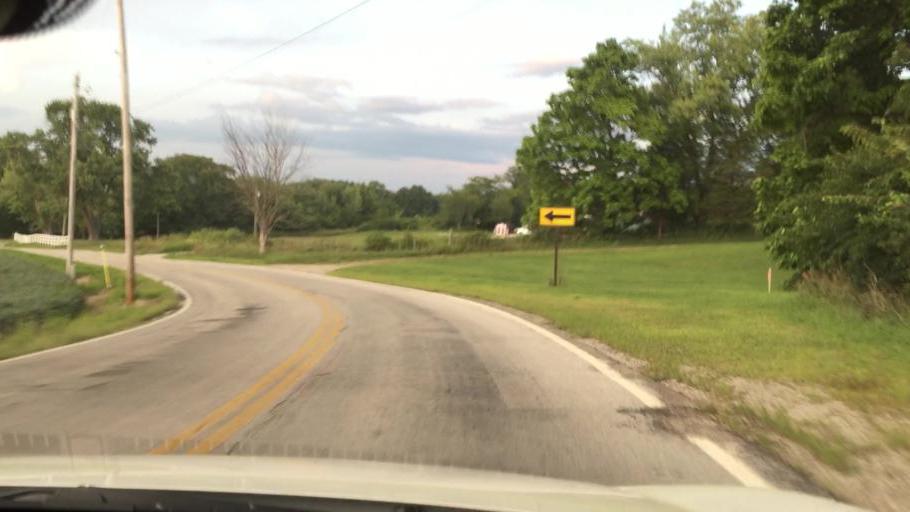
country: US
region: Ohio
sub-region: Clark County
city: Northridge
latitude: 39.9879
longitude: -83.6651
